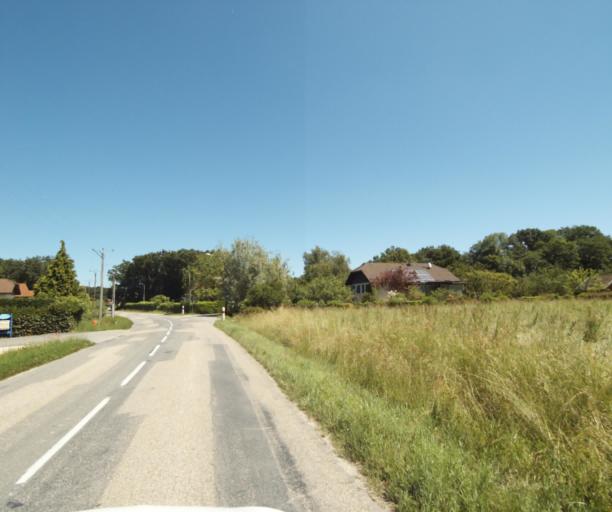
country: FR
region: Rhone-Alpes
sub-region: Departement de la Haute-Savoie
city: Veigy-Foncenex
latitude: 46.2802
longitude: 6.2606
